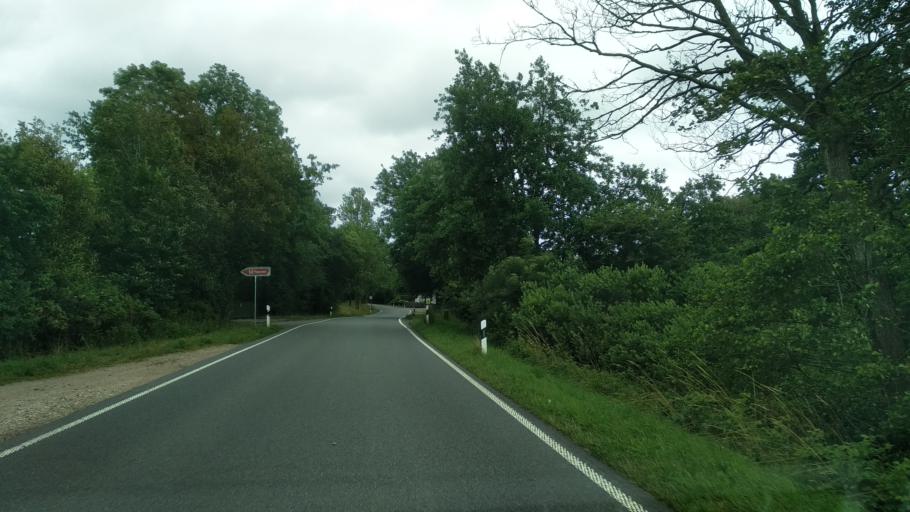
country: DE
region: Schleswig-Holstein
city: Sieverstedt
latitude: 54.6085
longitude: 9.4750
